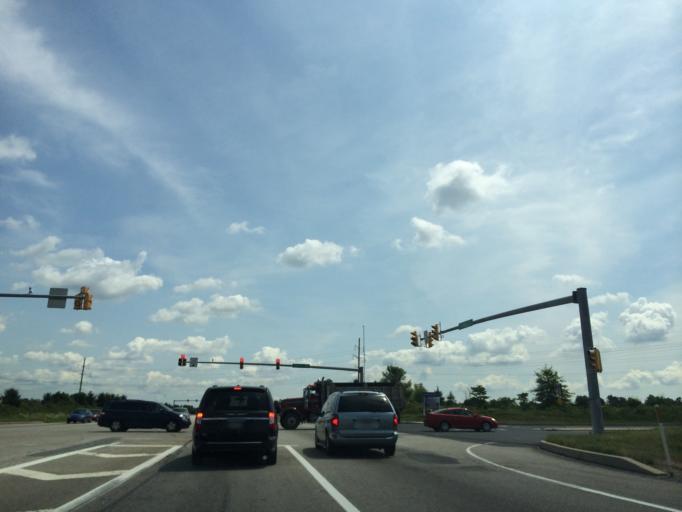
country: US
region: Pennsylvania
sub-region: Lehigh County
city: Wescosville
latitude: 40.5657
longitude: -75.5651
